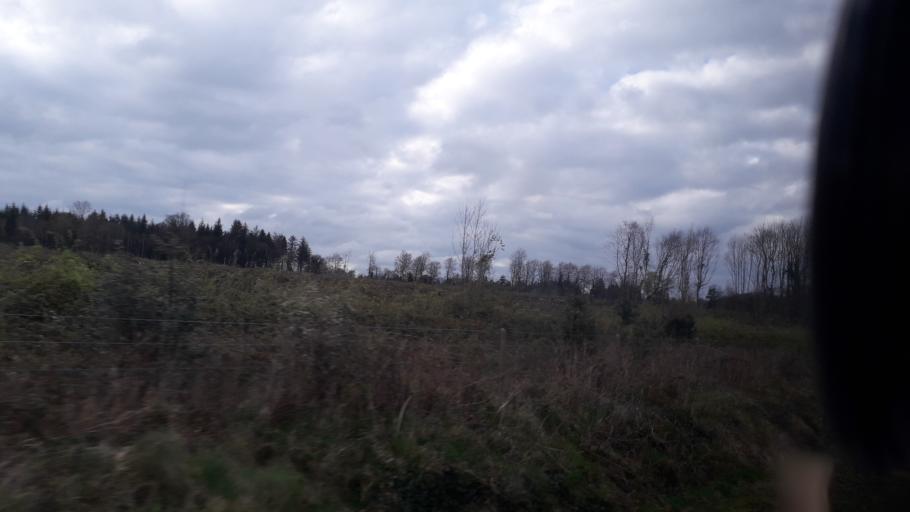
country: IE
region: Leinster
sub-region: An Iarmhi
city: An Muileann gCearr
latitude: 53.5935
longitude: -7.3894
